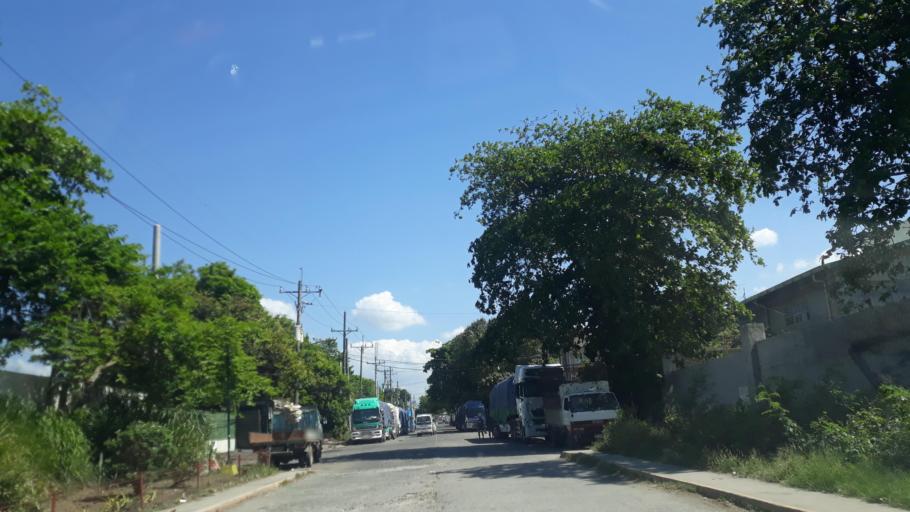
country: PH
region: Calabarzon
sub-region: Province of Cavite
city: Manggahan
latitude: 14.2973
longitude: 120.9176
